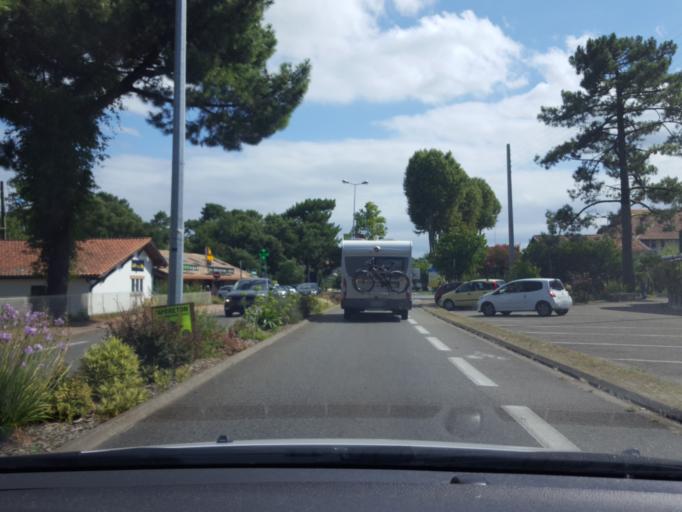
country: FR
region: Aquitaine
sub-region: Departement des Landes
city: Capbreton
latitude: 43.6426
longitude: -1.4259
